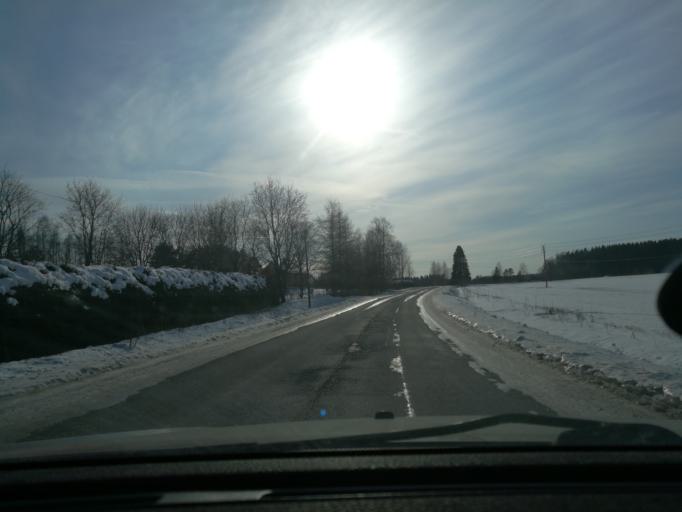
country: FI
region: Uusimaa
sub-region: Helsinki
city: Kaerkoelae
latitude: 60.5014
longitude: 23.9633
